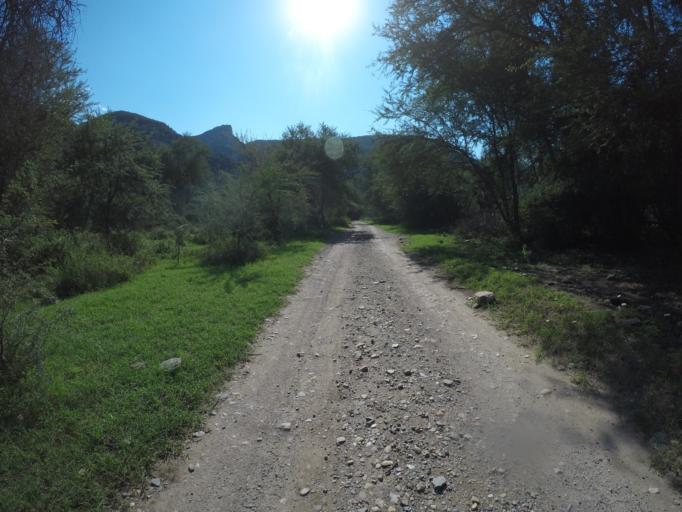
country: ZA
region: Eastern Cape
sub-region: Cacadu District Municipality
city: Kareedouw
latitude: -33.6561
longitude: 24.3657
